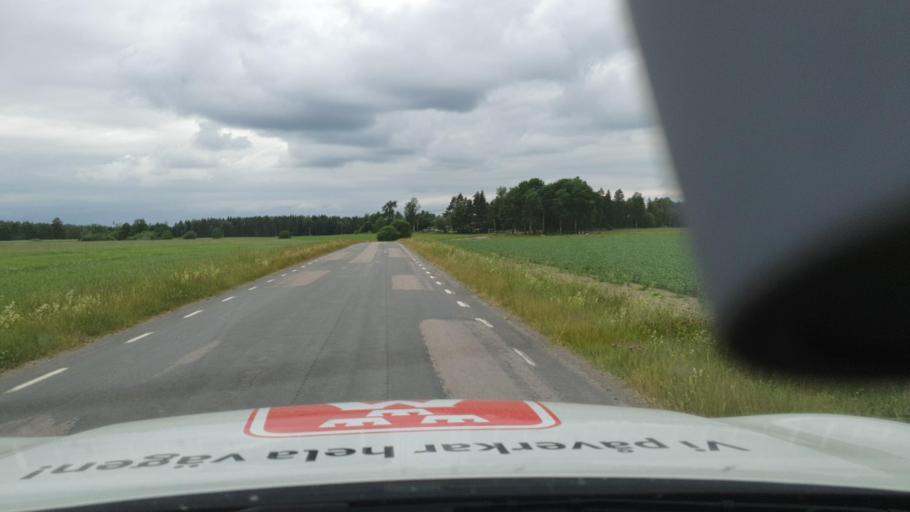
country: SE
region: Vaestra Goetaland
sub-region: Tidaholms Kommun
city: Olofstorp
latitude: 58.3028
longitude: 14.0386
